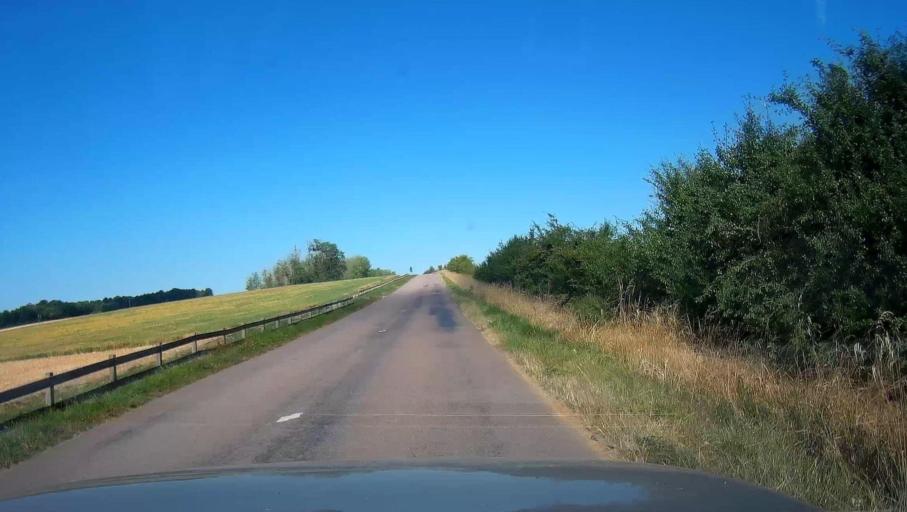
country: FR
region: Champagne-Ardenne
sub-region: Departement de la Haute-Marne
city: Langres
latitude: 47.8750
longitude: 5.3787
